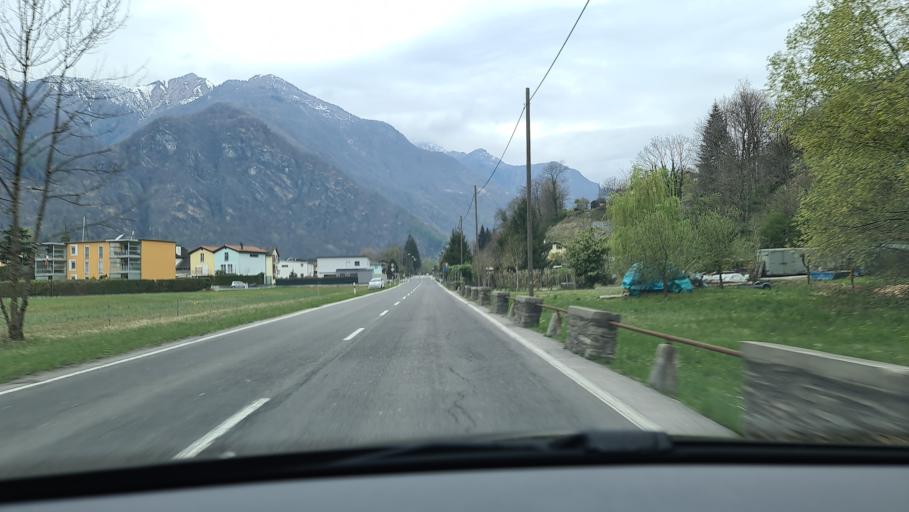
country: CH
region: Ticino
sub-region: Locarno District
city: Verscio
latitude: 46.2324
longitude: 8.7319
